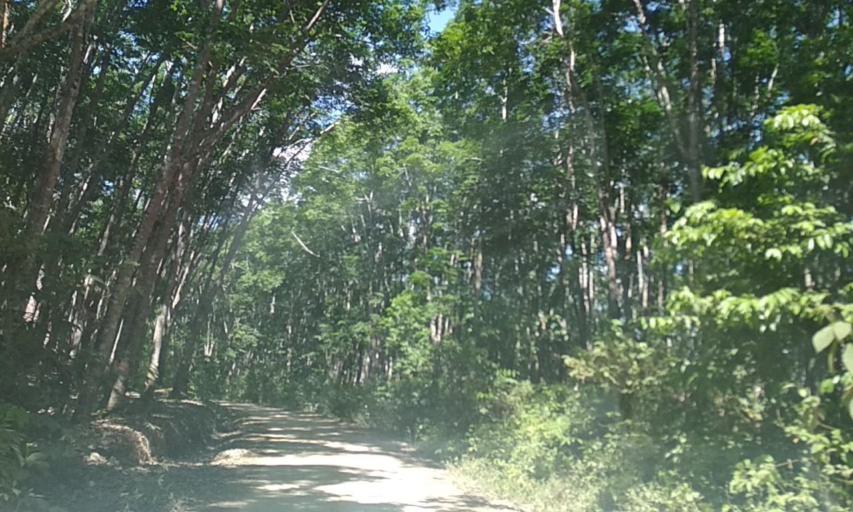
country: MX
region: Veracruz
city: Las Choapas
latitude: 17.7930
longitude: -94.1465
